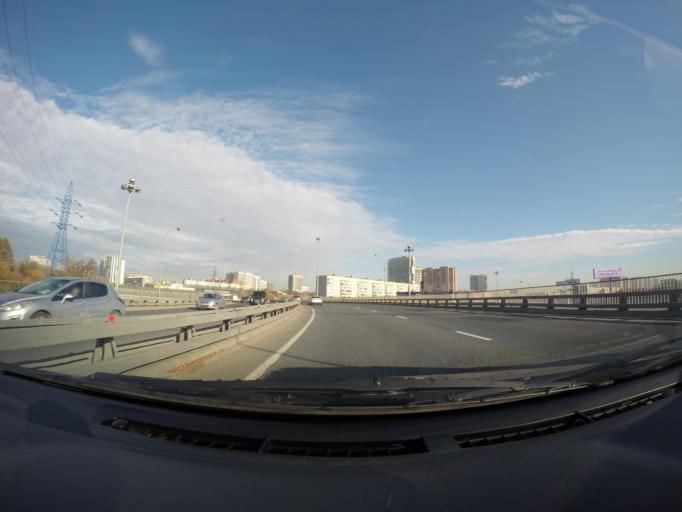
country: RU
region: Moskovskaya
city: Druzhba
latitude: 55.9097
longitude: 37.7769
